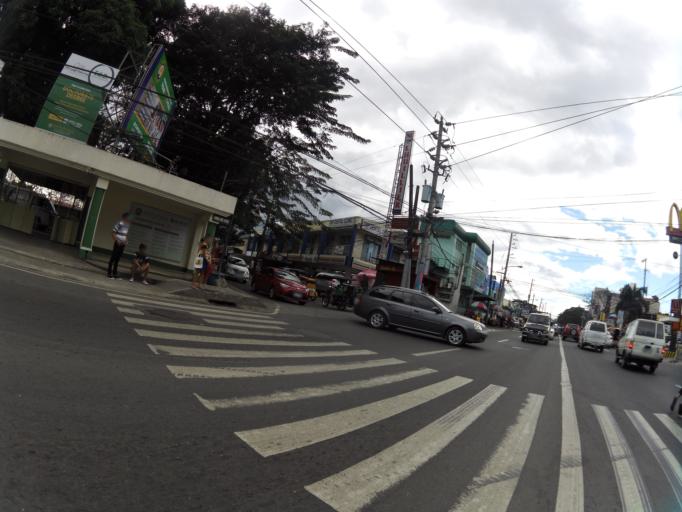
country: PH
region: Calabarzon
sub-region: Province of Rizal
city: Antipolo
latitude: 14.6335
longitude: 121.1090
